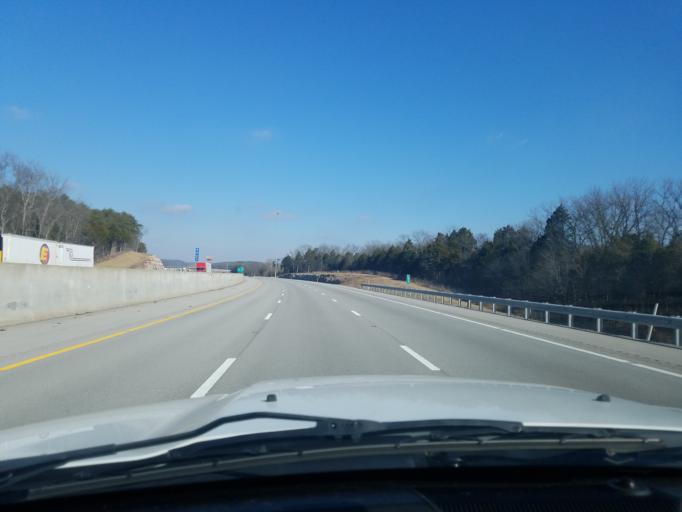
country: US
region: Kentucky
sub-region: Hart County
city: Horse Cave
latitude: 37.1926
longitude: -85.9392
